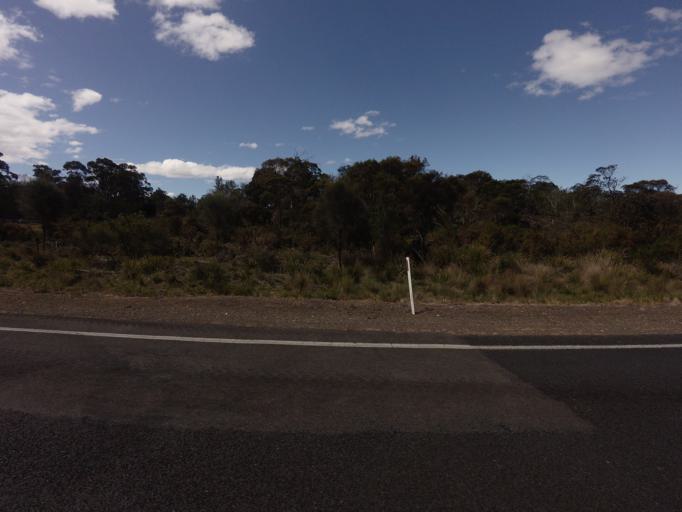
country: AU
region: Tasmania
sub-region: Break O'Day
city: St Helens
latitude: -42.0208
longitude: 148.0072
